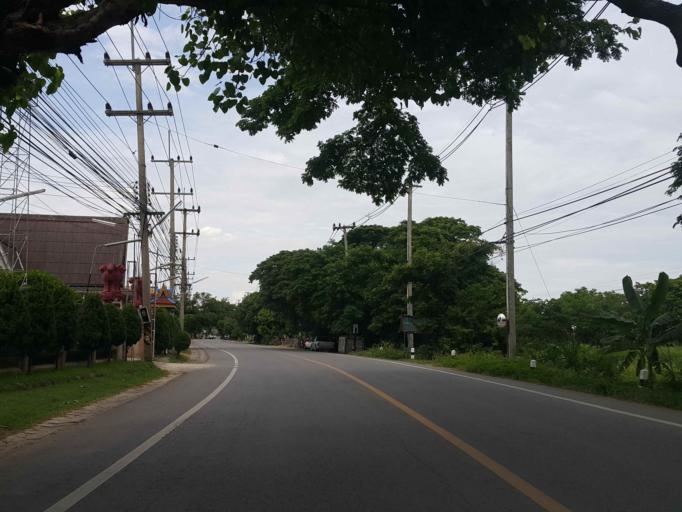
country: TH
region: Lamphun
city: Lamphun
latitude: 18.6226
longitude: 99.0347
